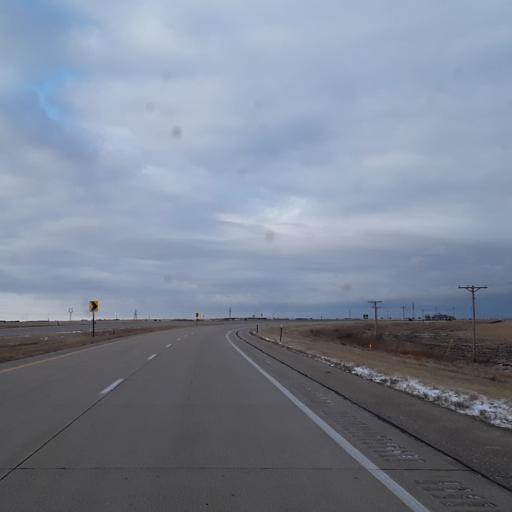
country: US
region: Nebraska
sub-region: Fillmore County
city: Geneva
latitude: 40.4172
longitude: -97.5951
